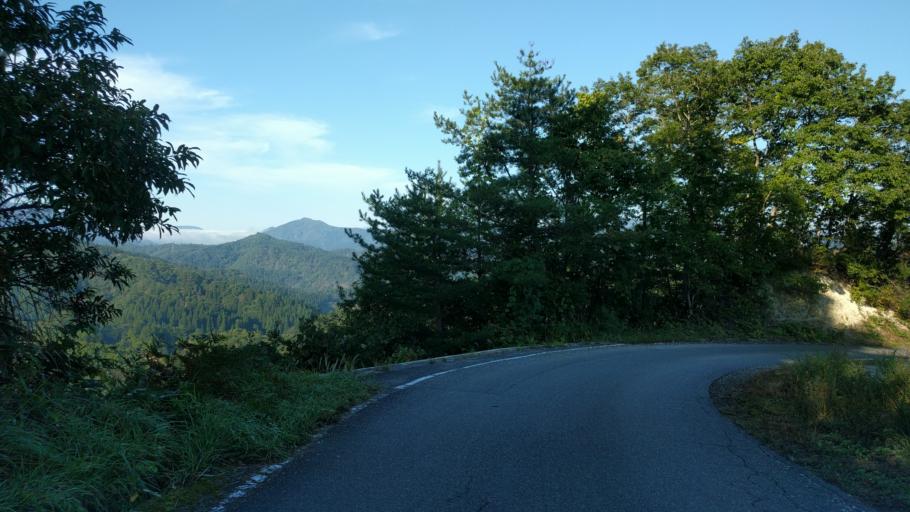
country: JP
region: Fukushima
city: Kitakata
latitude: 37.4846
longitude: 139.7179
